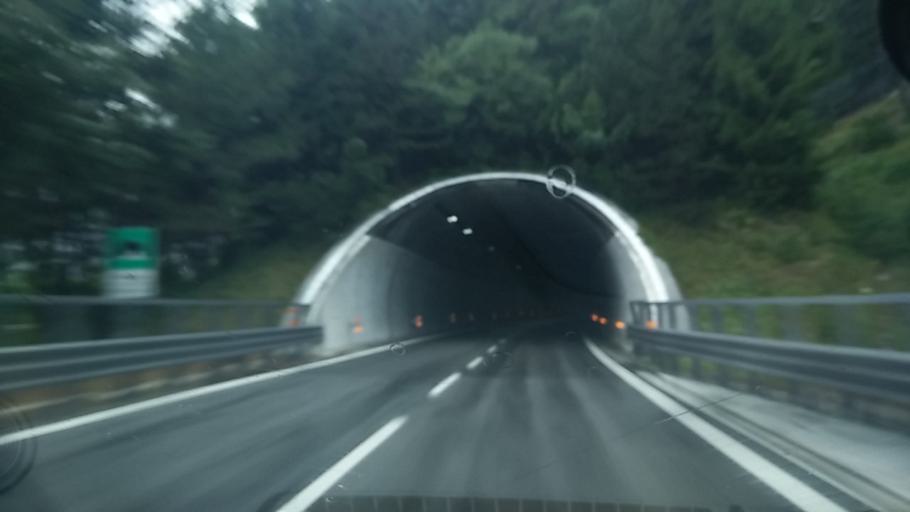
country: IT
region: Friuli Venezia Giulia
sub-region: Provincia di Udine
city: Malborghetto
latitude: 46.5028
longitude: 13.5009
